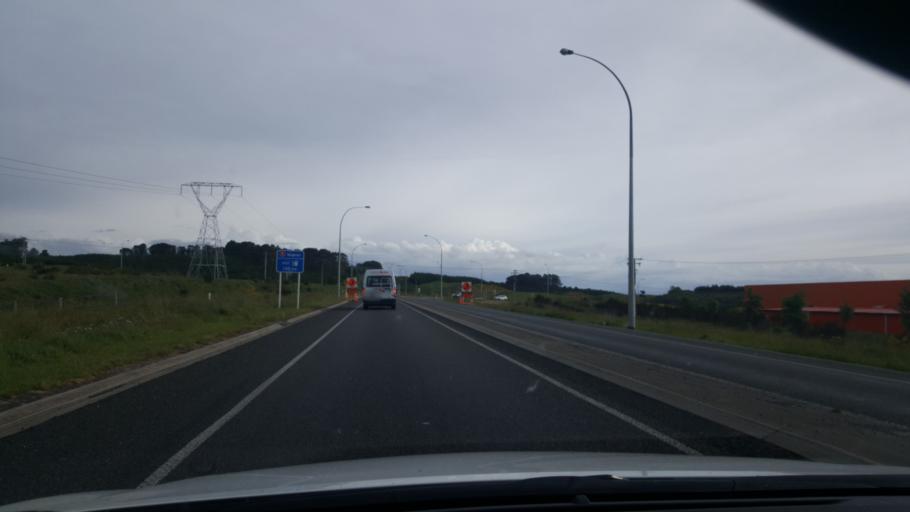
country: NZ
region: Waikato
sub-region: Taupo District
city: Taupo
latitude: -38.7024
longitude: 176.1119
